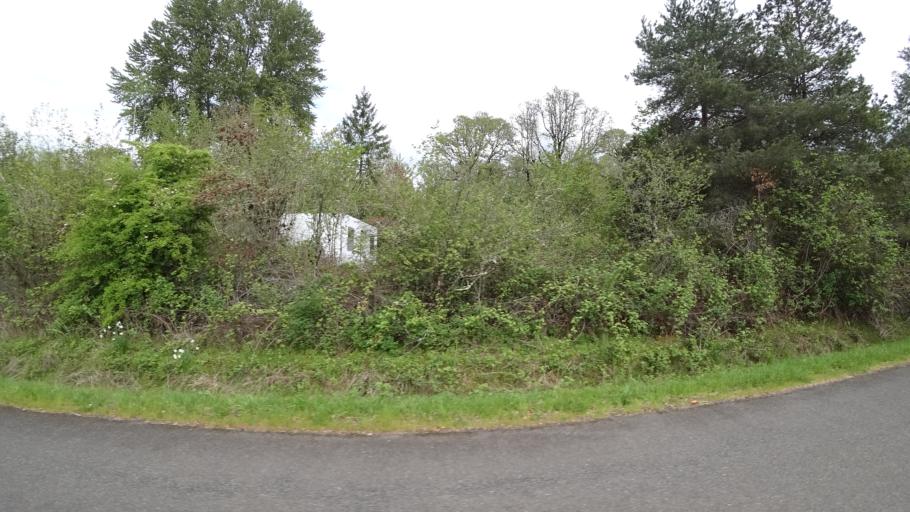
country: US
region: Oregon
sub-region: Washington County
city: Hillsboro
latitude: 45.5553
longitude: -122.9528
